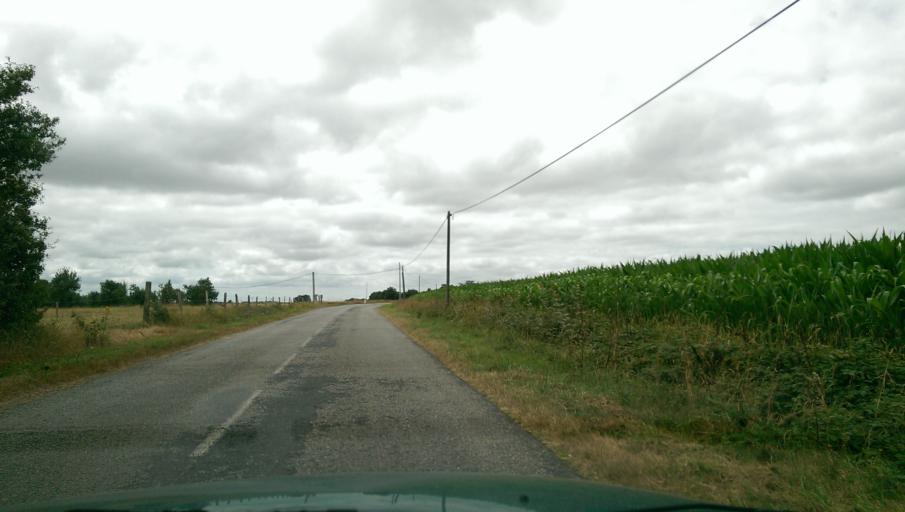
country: FR
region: Pays de la Loire
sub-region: Departement de la Loire-Atlantique
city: Remouille
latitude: 47.0407
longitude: -1.3959
